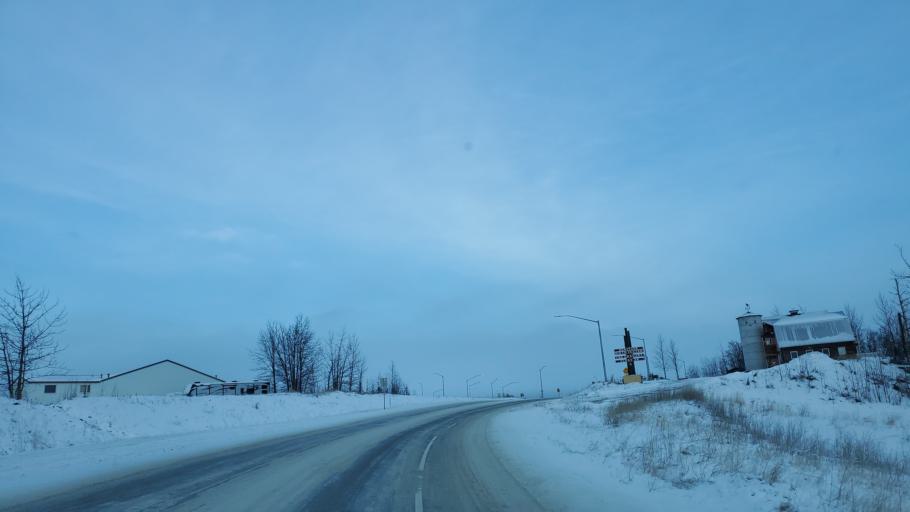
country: US
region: Alaska
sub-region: Matanuska-Susitna Borough
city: Gateway
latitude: 61.5607
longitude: -149.2714
